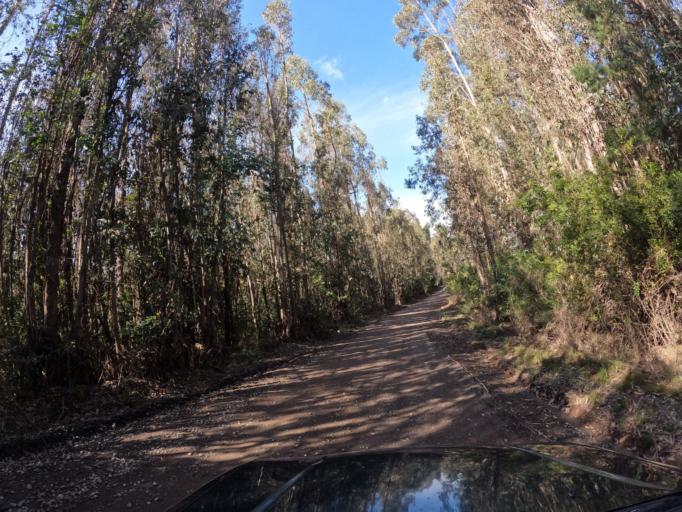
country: CL
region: Biobio
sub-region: Provincia de Biobio
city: La Laja
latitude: -37.0832
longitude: -72.7870
